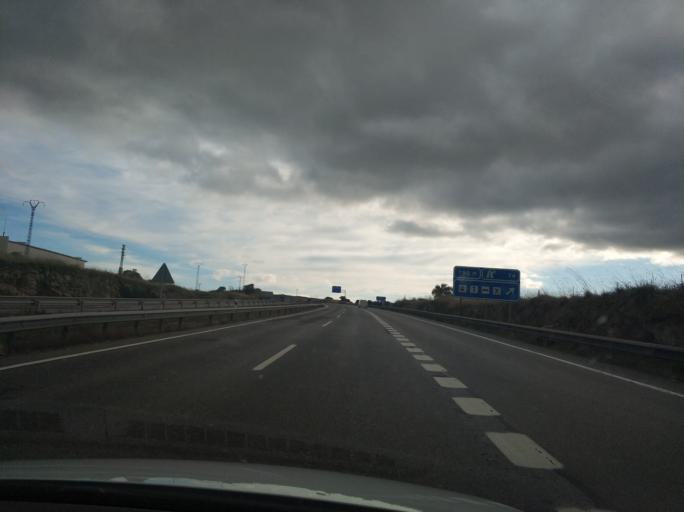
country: ES
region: Madrid
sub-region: Provincia de Madrid
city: Buitrago del Lozoya
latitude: 40.9914
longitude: -3.6424
